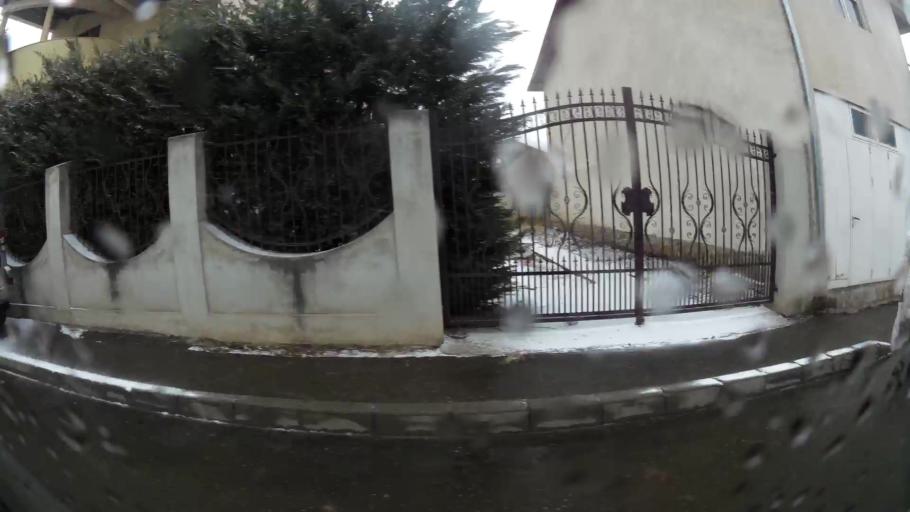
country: RO
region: Prahova
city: Ploiesti
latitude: 44.9461
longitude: 26.0050
